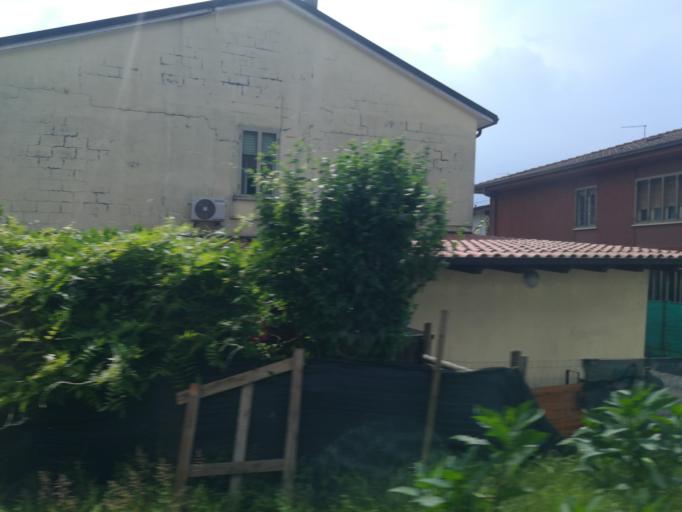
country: IT
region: Veneto
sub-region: Provincia di Vicenza
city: Dueville
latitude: 45.6330
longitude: 11.5481
